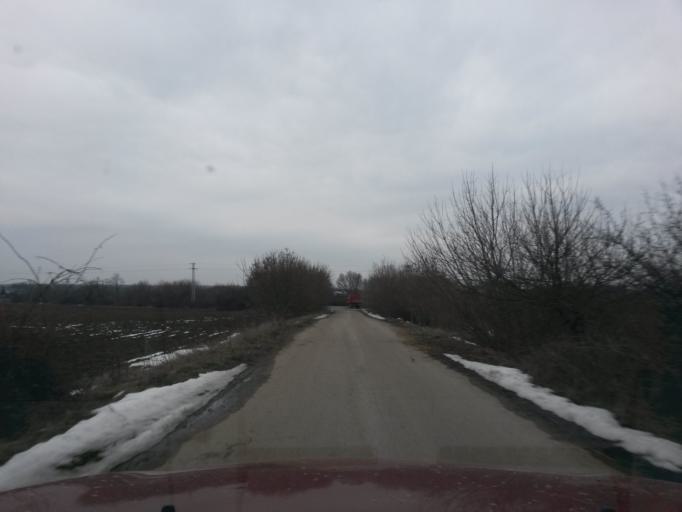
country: SK
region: Kosicky
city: Michalovce
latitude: 48.7291
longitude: 21.8704
